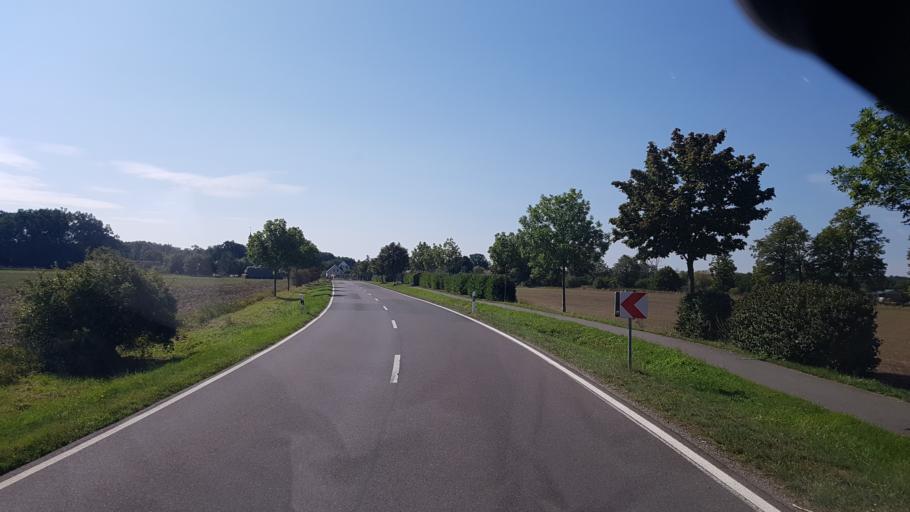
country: DE
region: Brandenburg
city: Altdobern
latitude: 51.7183
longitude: 14.0395
